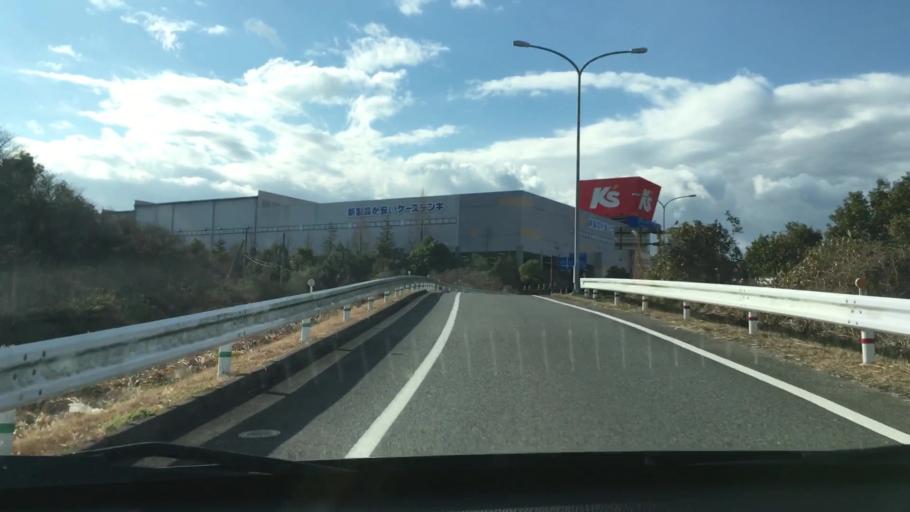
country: JP
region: Oita
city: Tsurusaki
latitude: 33.1954
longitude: 131.6626
